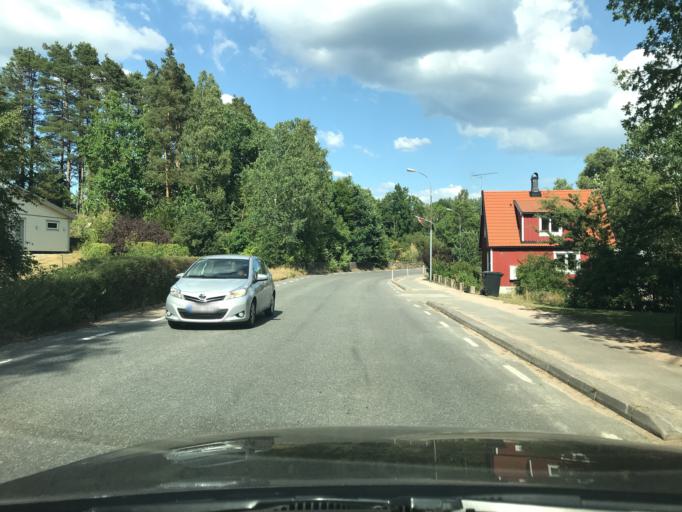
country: SE
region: Skane
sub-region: Hassleholms Kommun
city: Hastveda
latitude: 56.2864
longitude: 13.9275
